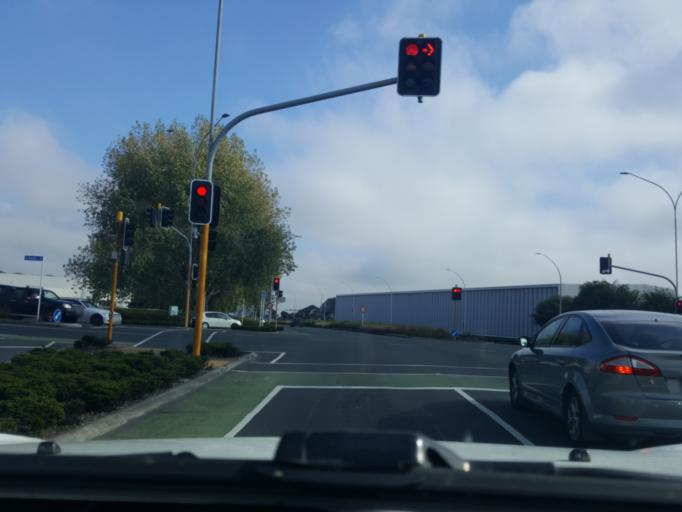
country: NZ
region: Waikato
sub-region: Hamilton City
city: Hamilton
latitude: -37.7479
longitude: 175.2406
